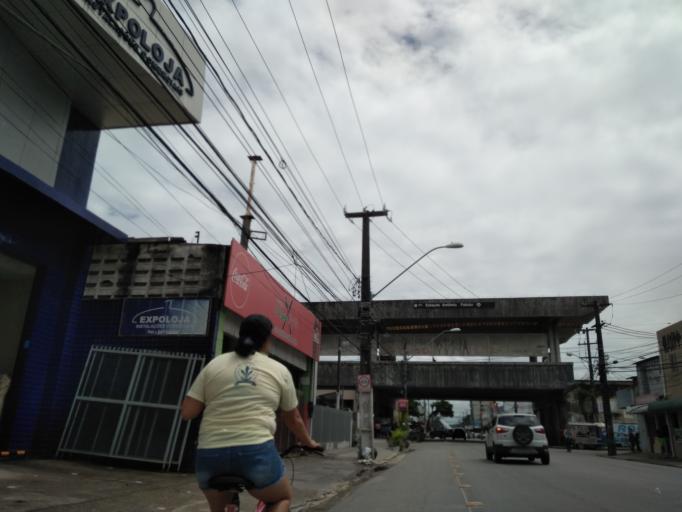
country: BR
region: Pernambuco
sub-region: Recife
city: Recife
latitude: -8.1097
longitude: -34.9084
